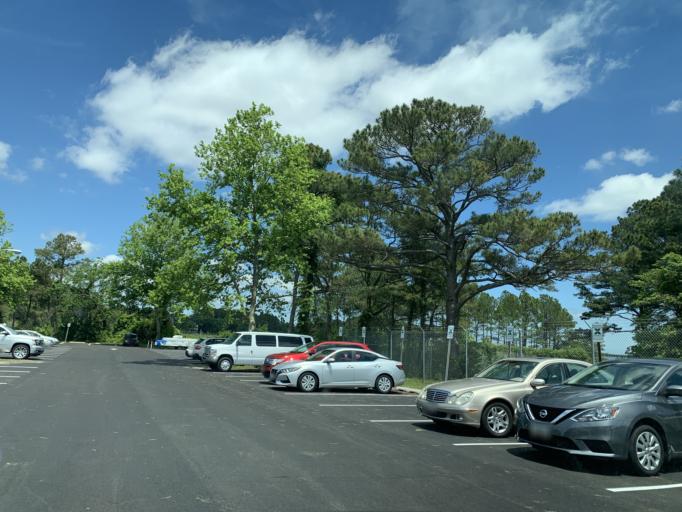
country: US
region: Maryland
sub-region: Worcester County
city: West Ocean City
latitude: 38.3105
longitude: -75.1179
